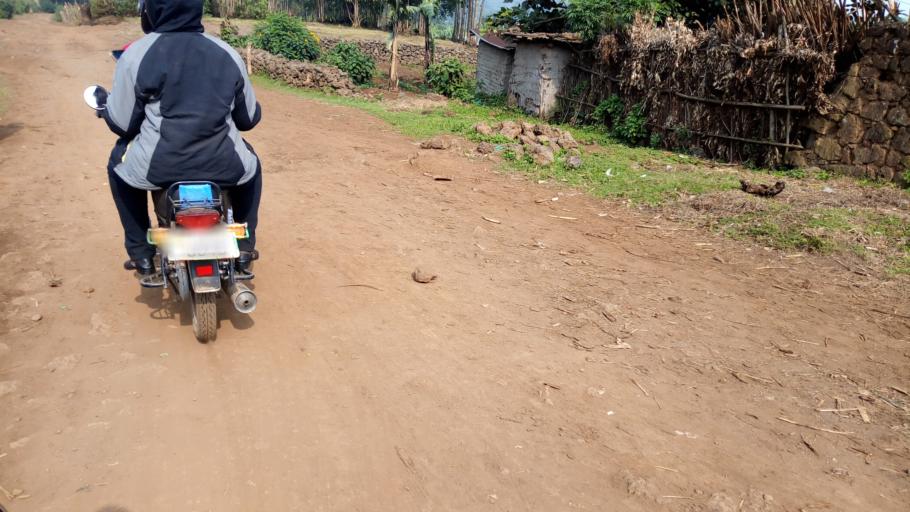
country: UG
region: Western Region
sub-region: Kisoro District
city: Kisoro
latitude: -1.3097
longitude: 29.6579
